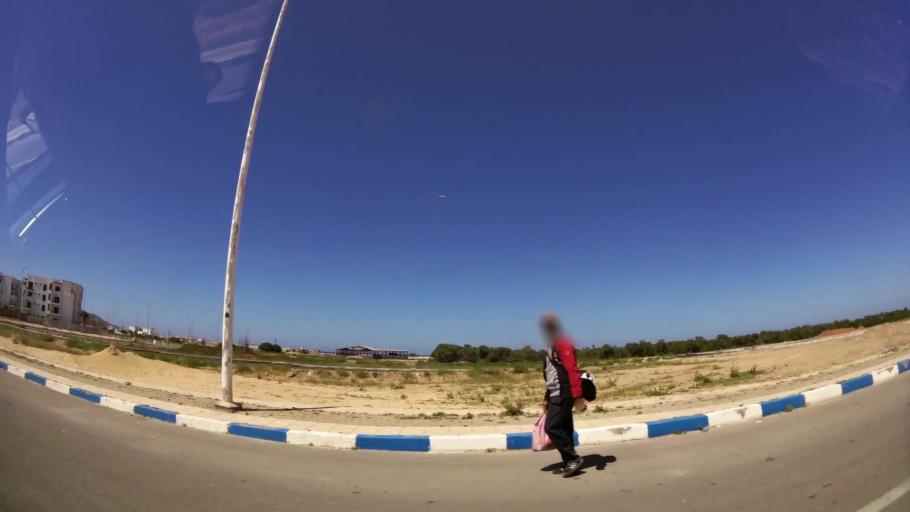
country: MA
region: Oriental
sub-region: Berkane-Taourirt
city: Madagh
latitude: 35.1378
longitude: -2.4193
